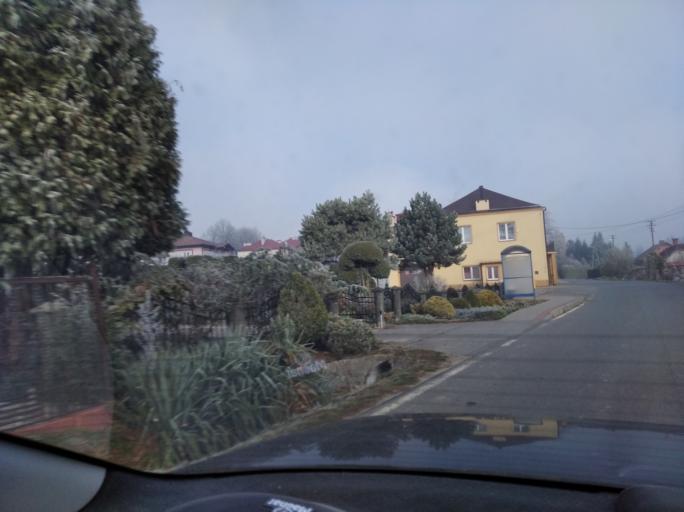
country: PL
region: Subcarpathian Voivodeship
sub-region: Powiat strzyzowski
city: Wysoka Strzyzowska
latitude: 49.8518
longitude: 21.7318
